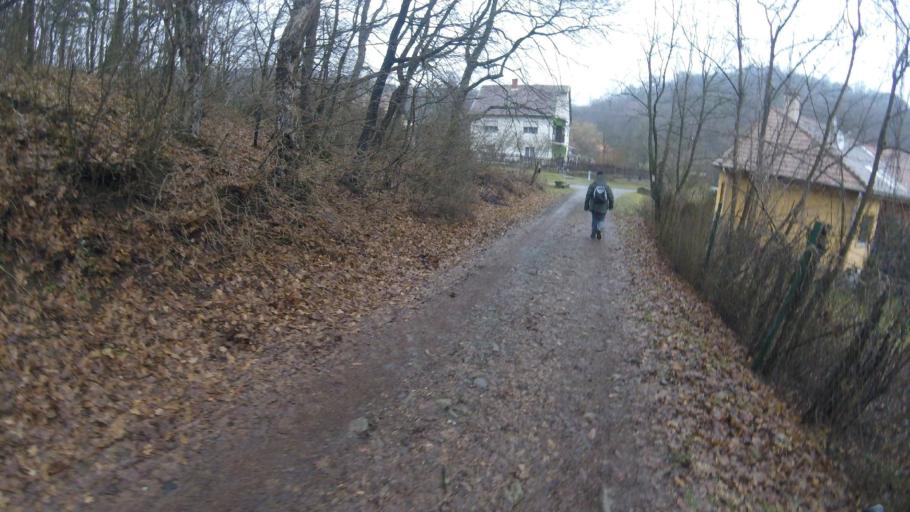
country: HU
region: Borsod-Abauj-Zemplen
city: Saly
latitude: 47.9816
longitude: 20.6342
